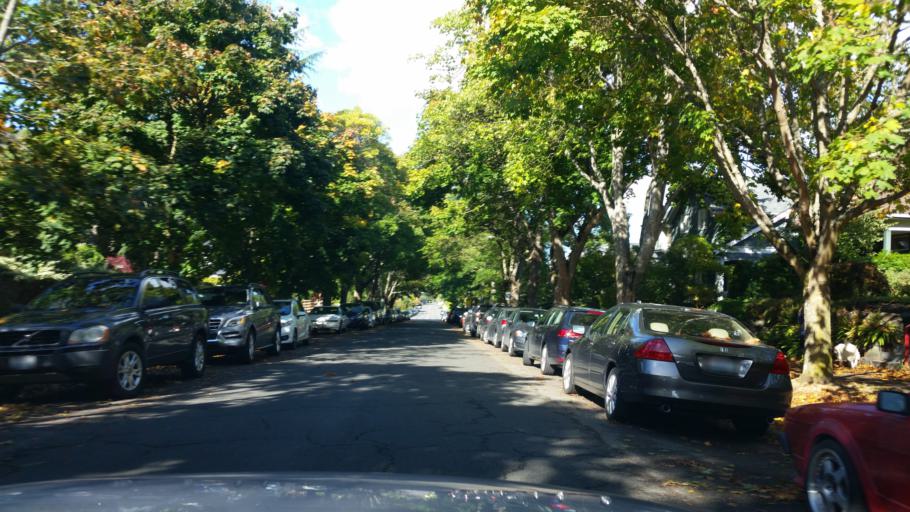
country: US
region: Washington
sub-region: King County
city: Seattle
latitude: 47.6381
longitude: -122.3663
